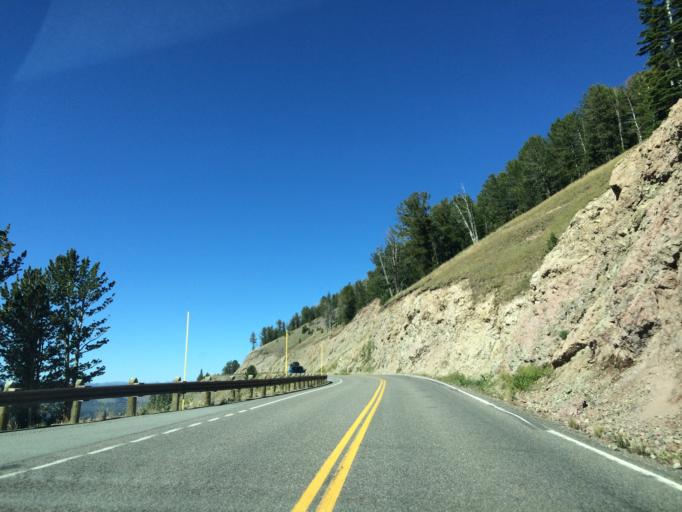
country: US
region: Montana
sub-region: Gallatin County
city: West Yellowstone
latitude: 44.7880
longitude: -110.4526
